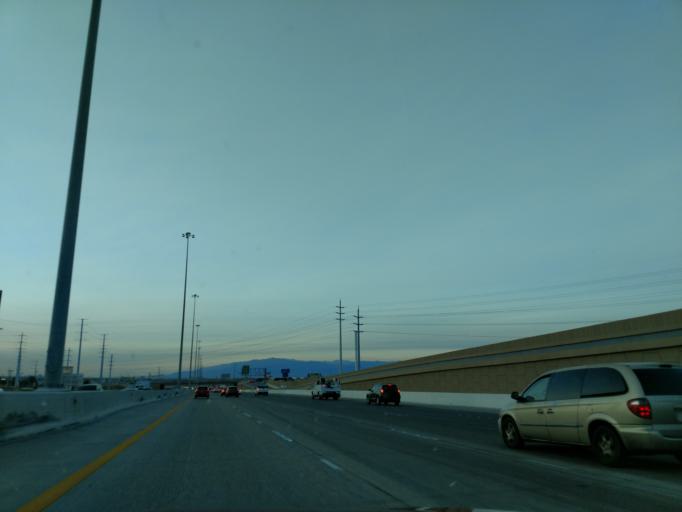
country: US
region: Nevada
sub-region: Clark County
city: Whitney
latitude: 36.0677
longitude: -115.0342
